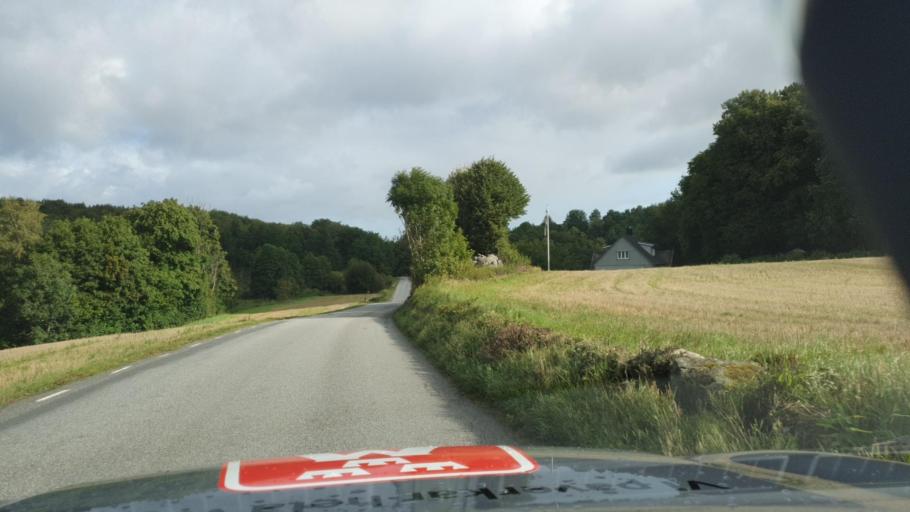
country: SE
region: Skane
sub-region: Hassleholms Kommun
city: Vinslov
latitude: 56.0735
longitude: 13.8418
